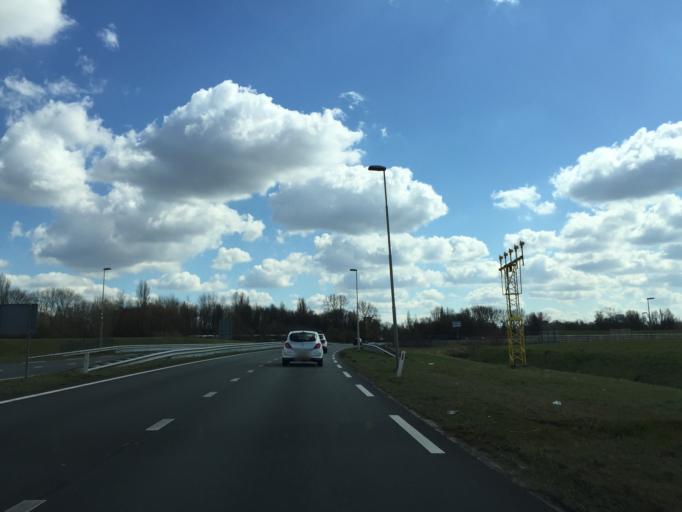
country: NL
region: South Holland
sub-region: Gemeente Lansingerland
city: Berkel en Rodenrijs
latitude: 51.9650
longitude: 4.4597
